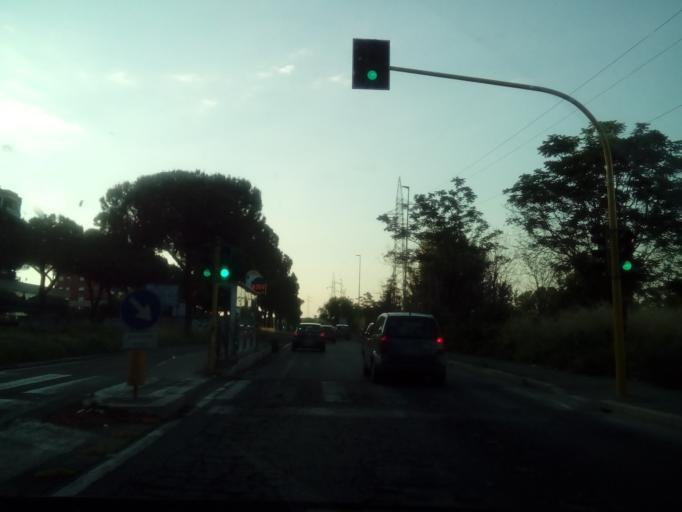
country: IT
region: Latium
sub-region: Citta metropolitana di Roma Capitale
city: Rome
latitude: 41.9162
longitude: 12.5693
